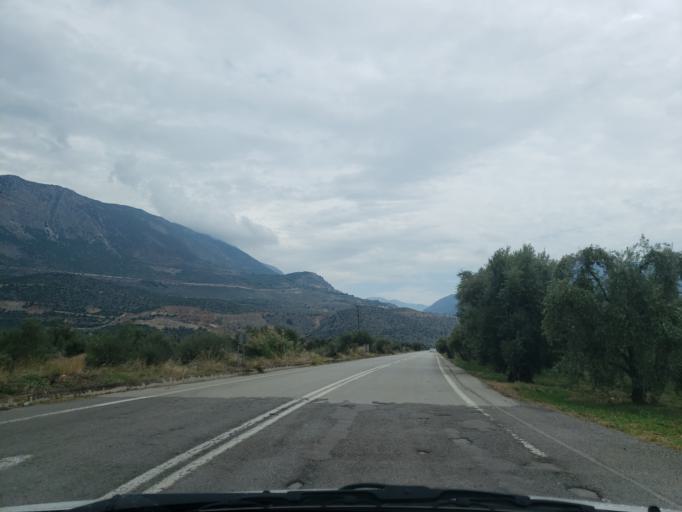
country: GR
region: Central Greece
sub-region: Nomos Fokidos
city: Kirra
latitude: 38.4807
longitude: 22.4355
